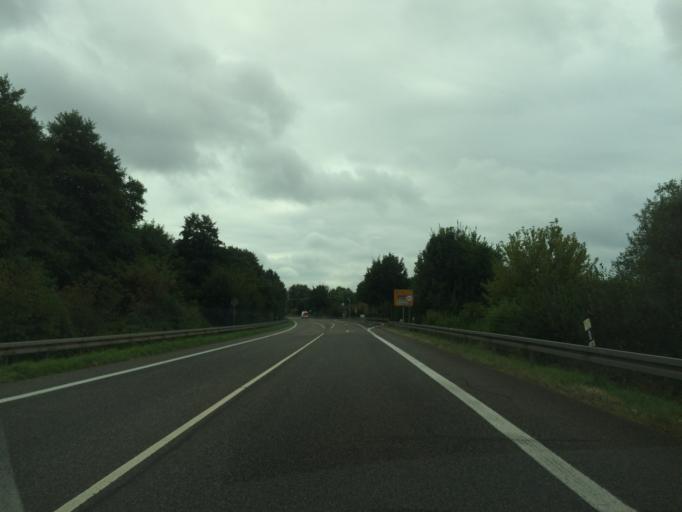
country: DE
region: Saarland
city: Rehlingen-Siersburg
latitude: 49.3725
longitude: 6.7074
